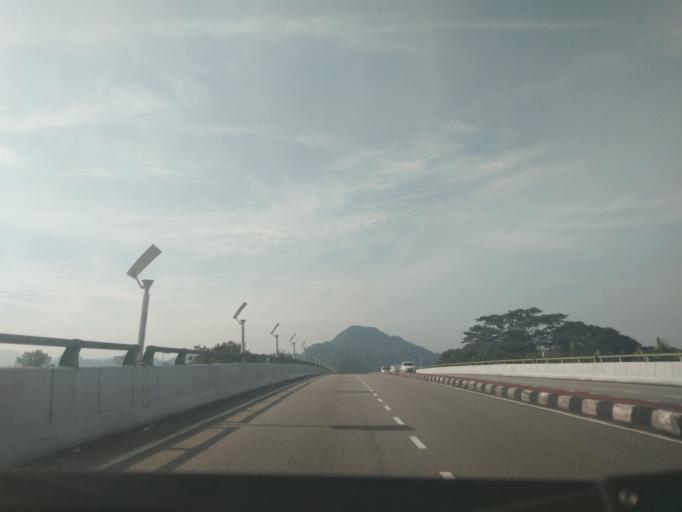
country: MY
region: Perak
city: Ipoh
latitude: 4.5820
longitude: 101.1028
